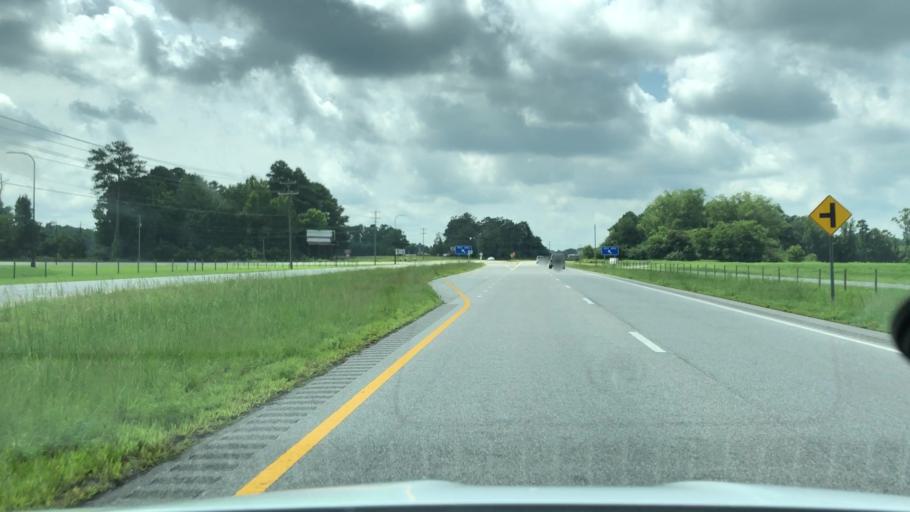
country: US
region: North Carolina
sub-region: Beaufort County
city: Washington
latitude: 35.4912
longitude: -77.1072
